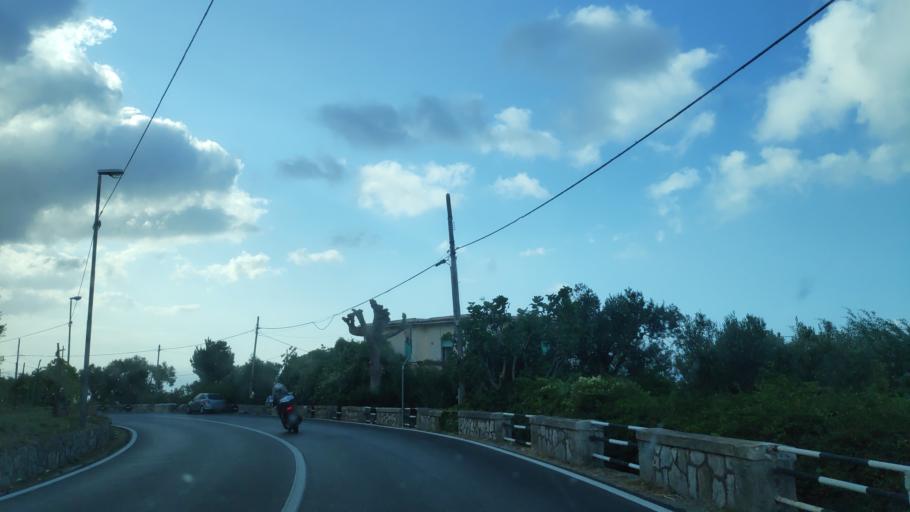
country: IT
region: Campania
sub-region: Provincia di Napoli
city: Piano di Sorrento
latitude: 40.6162
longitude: 14.4298
